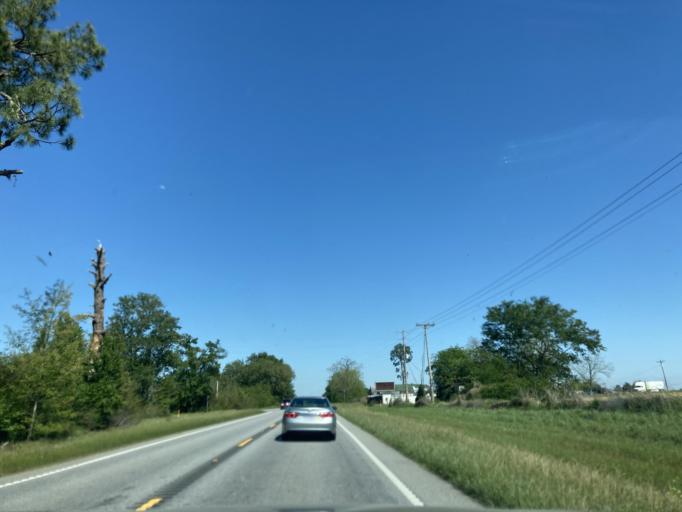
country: US
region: Georgia
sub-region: Miller County
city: Colquitt
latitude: 31.1864
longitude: -84.6351
